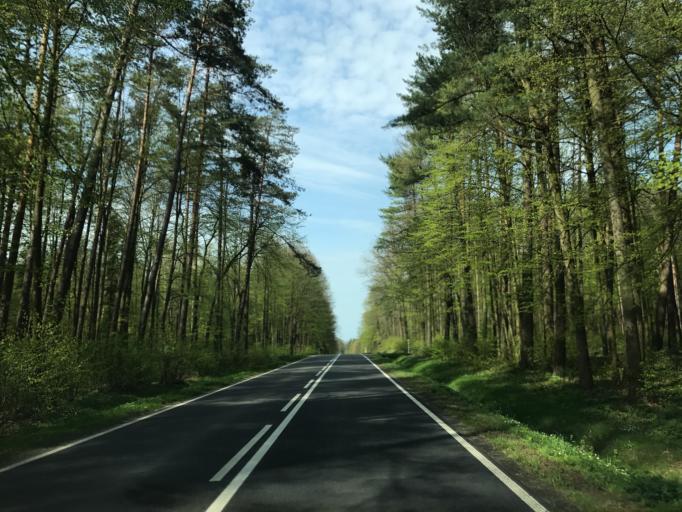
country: PL
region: Warmian-Masurian Voivodeship
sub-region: Powiat dzialdowski
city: Lidzbark
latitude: 53.3285
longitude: 19.8170
